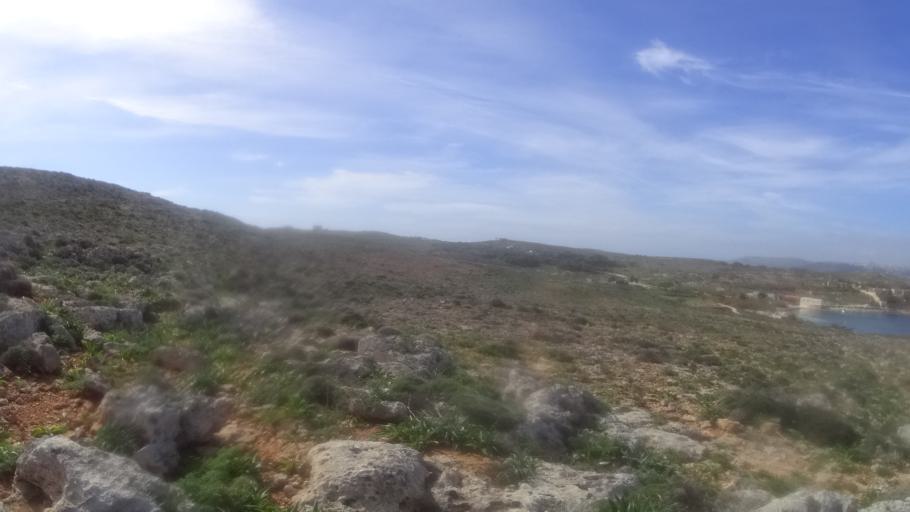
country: MT
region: Il-Qala
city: Qala
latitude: 36.0161
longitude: 14.3408
